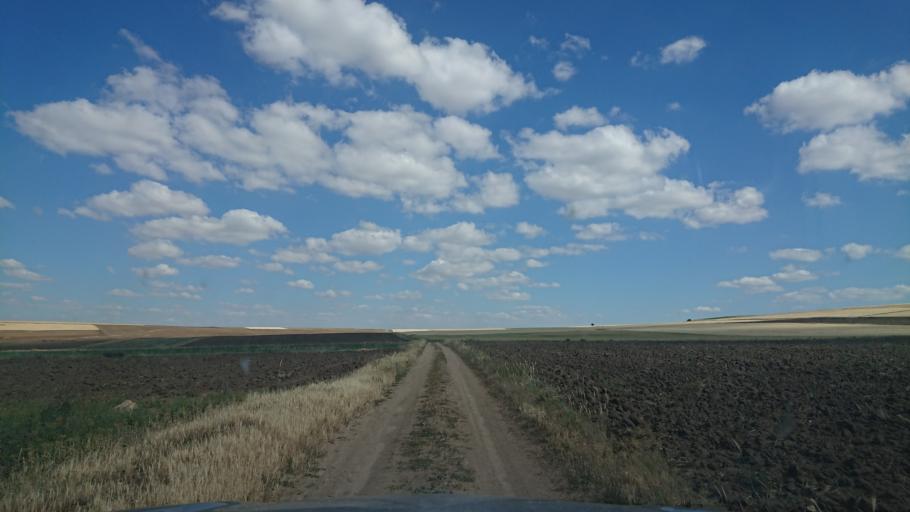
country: TR
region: Aksaray
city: Sariyahsi
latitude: 38.9372
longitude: 33.8397
